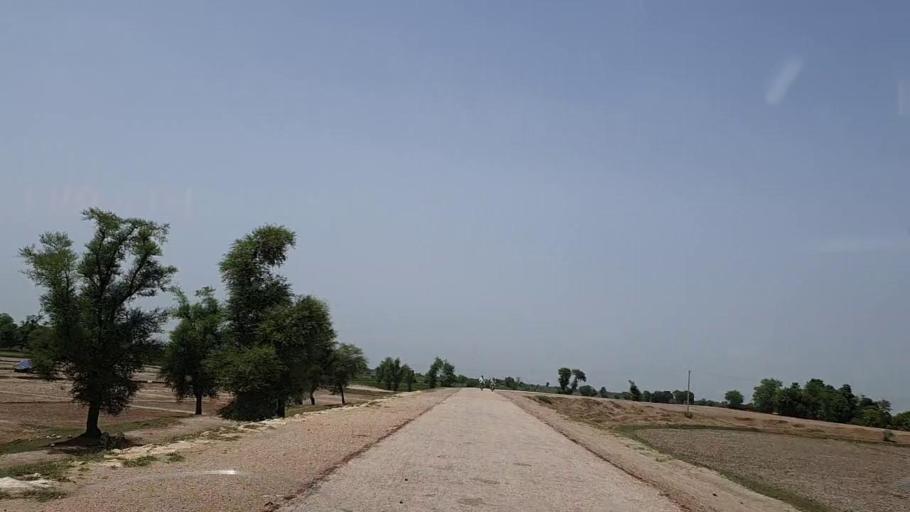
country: PK
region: Sindh
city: Tharu Shah
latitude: 27.0098
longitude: 68.1021
